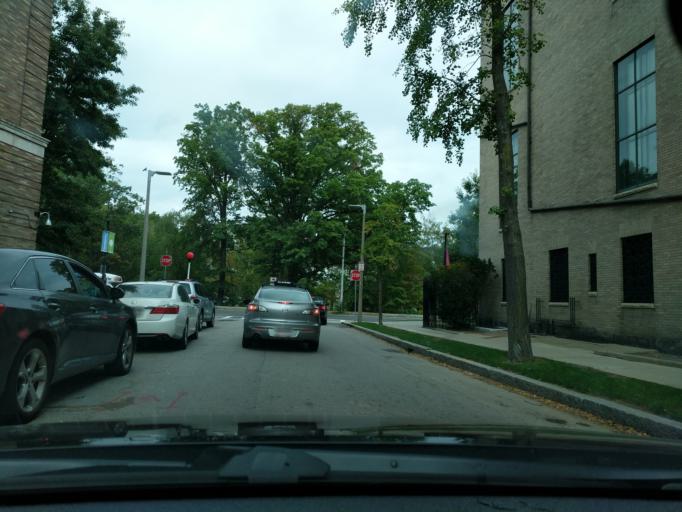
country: US
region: Massachusetts
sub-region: Norfolk County
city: Brookline
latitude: 42.3387
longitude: -71.0993
